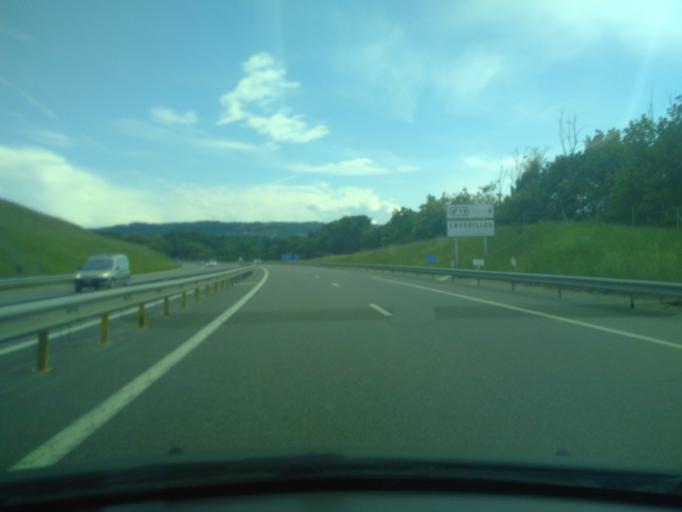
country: FR
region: Rhone-Alpes
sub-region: Departement de la Haute-Savoie
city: Feigeres
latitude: 46.1215
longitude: 6.0875
